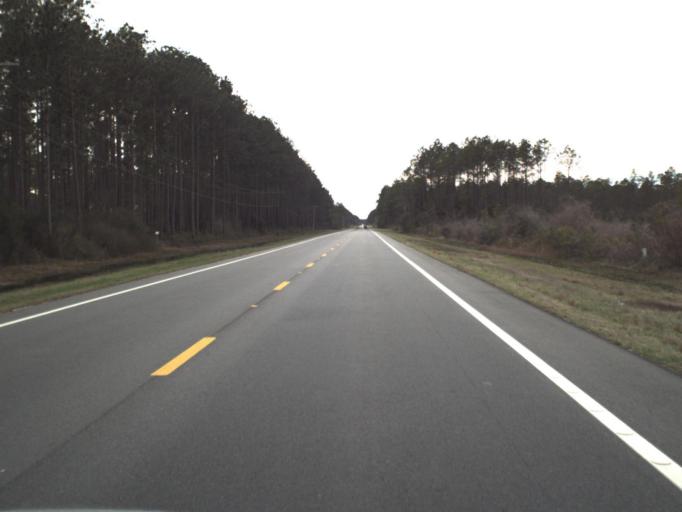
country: US
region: Florida
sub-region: Gulf County
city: Wewahitchka
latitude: 30.1419
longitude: -85.2784
